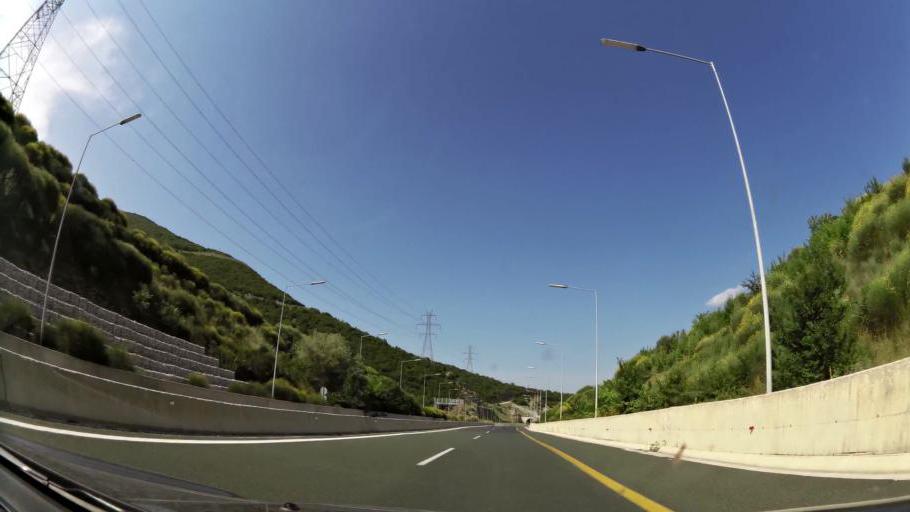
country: GR
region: Central Macedonia
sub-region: Nomos Imathias
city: Rizomata
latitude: 40.3971
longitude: 22.1620
